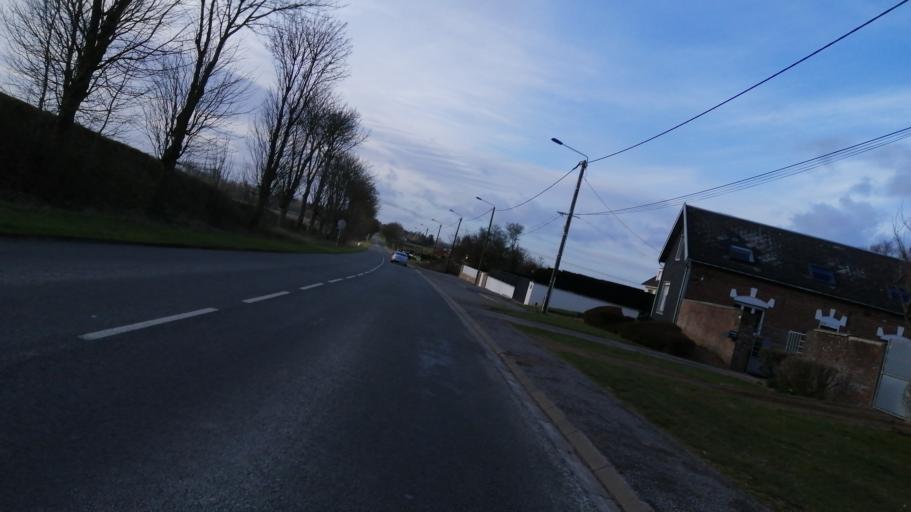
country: FR
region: Nord-Pas-de-Calais
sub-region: Departement du Pas-de-Calais
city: Beaurains
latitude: 50.2496
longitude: 2.8115
